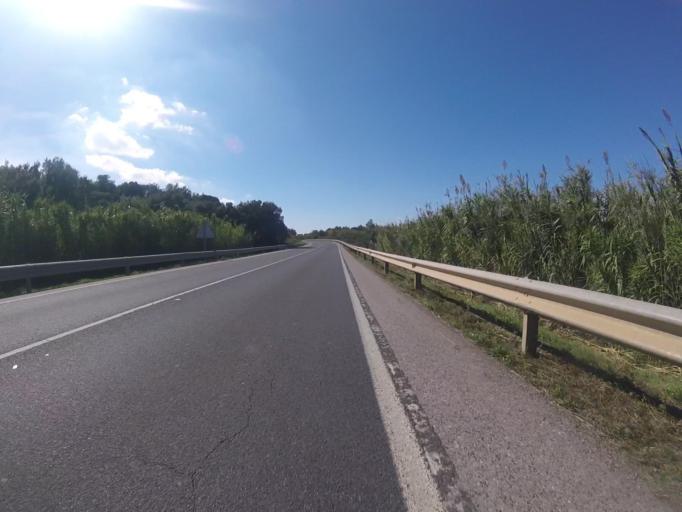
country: ES
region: Valencia
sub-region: Provincia de Castello
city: Sarratella
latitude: 40.3319
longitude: -0.0145
